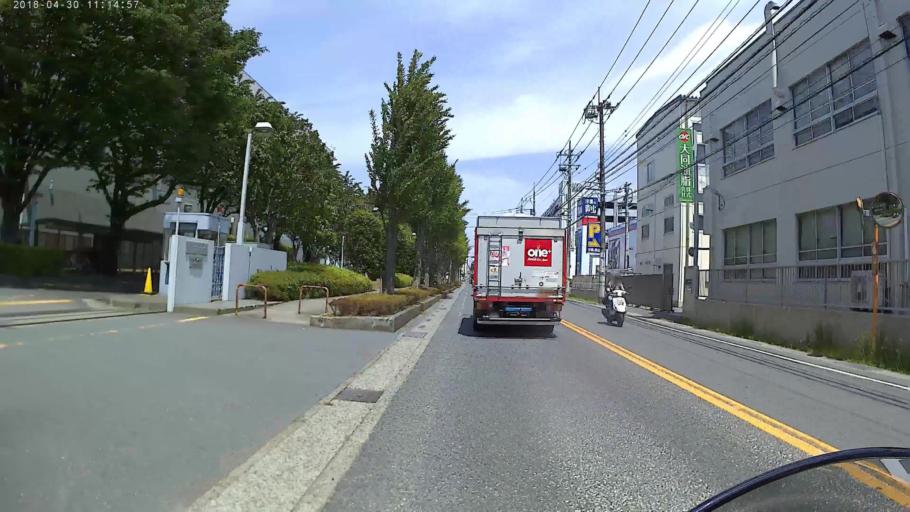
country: JP
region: Kanagawa
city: Minami-rinkan
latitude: 35.4776
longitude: 139.4316
